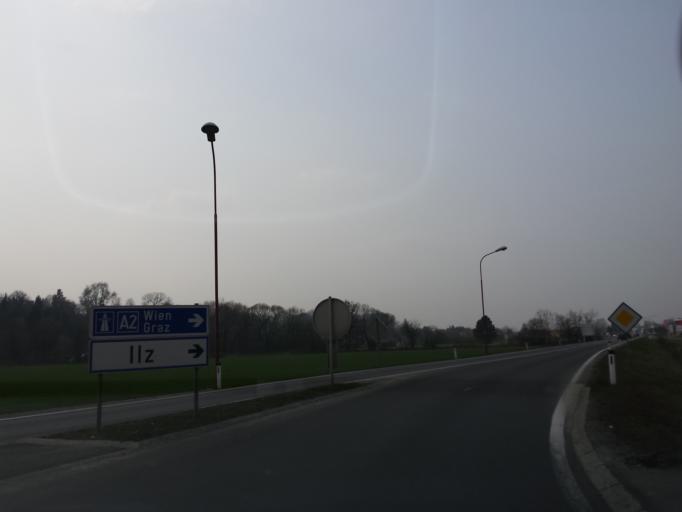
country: AT
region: Styria
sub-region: Politischer Bezirk Hartberg-Fuerstenfeld
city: Fuerstenfeld
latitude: 47.0530
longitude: 16.0810
